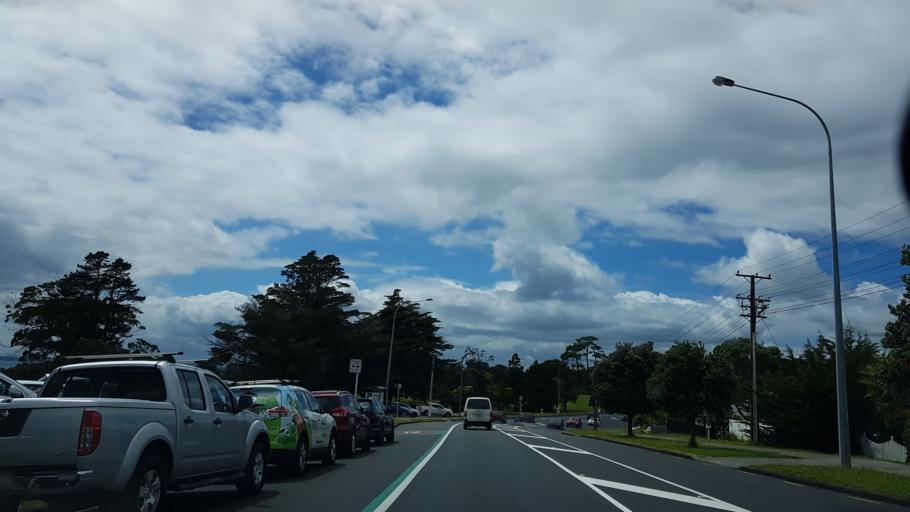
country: NZ
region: Auckland
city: Murrays Bay
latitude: -36.7524
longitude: 174.7495
